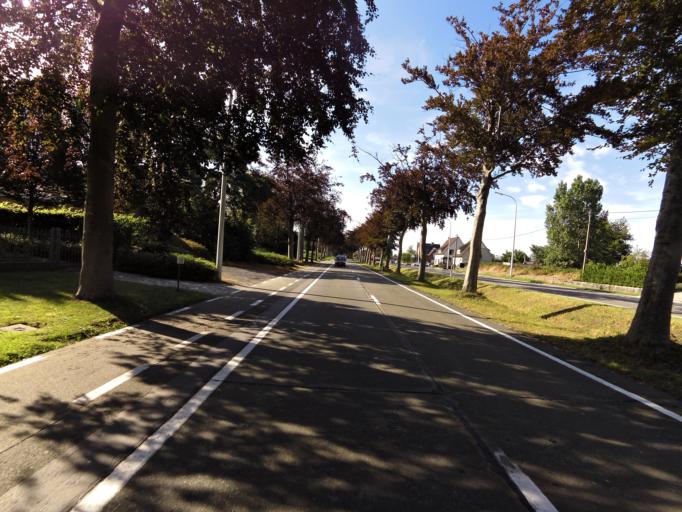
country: BE
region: Flanders
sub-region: Provincie Oost-Vlaanderen
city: Maldegem
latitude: 51.2121
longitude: 3.4203
